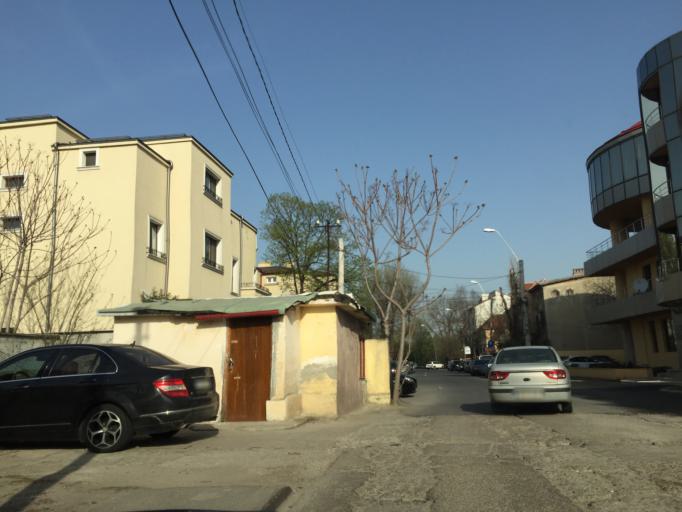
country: RO
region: Bucuresti
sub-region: Municipiul Bucuresti
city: Bucuresti
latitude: 44.4270
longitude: 26.0725
